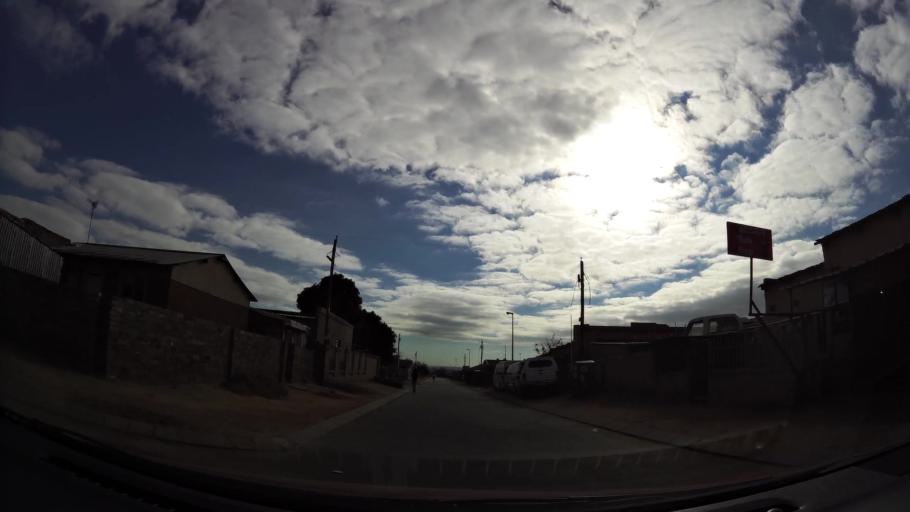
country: ZA
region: Gauteng
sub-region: City of Johannesburg Metropolitan Municipality
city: Modderfontein
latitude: -26.0413
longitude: 28.1859
